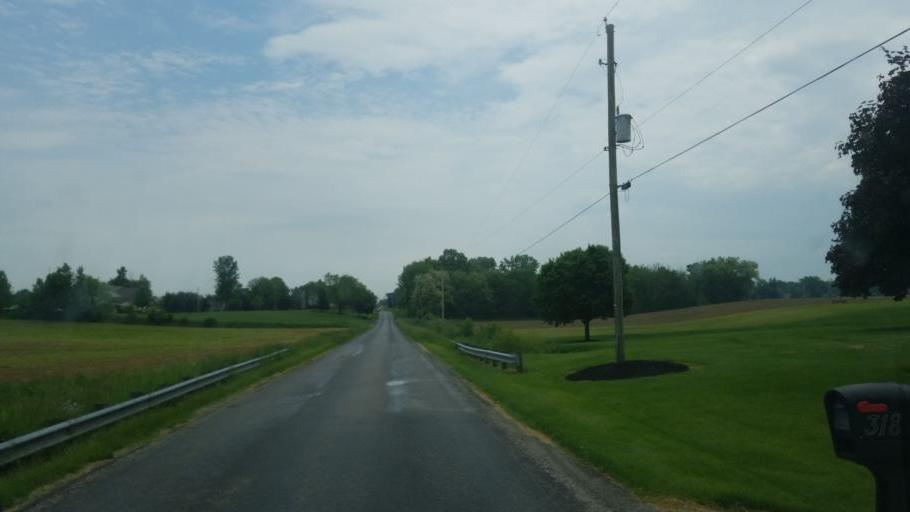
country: US
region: Ohio
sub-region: Wayne County
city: Orrville
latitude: 40.8017
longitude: -81.7553
